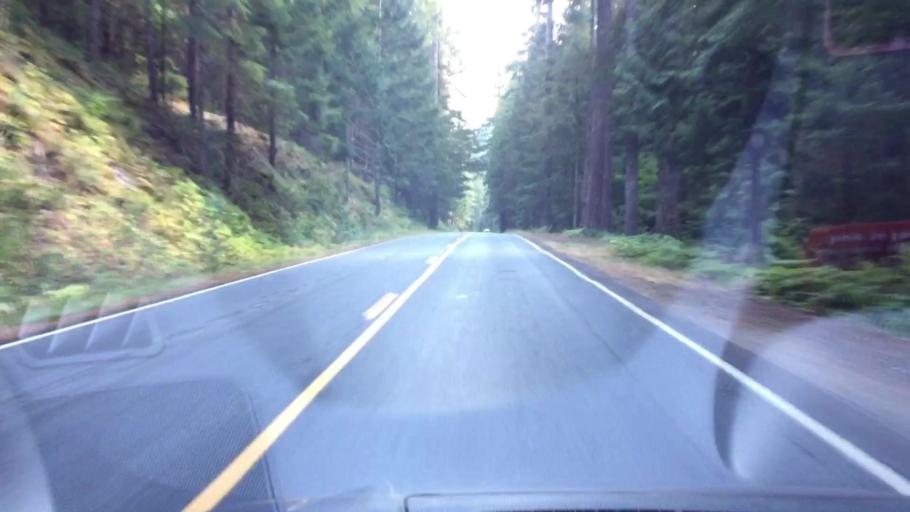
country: US
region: Washington
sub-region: Pierce County
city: Buckley
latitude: 46.7237
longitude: -121.5749
